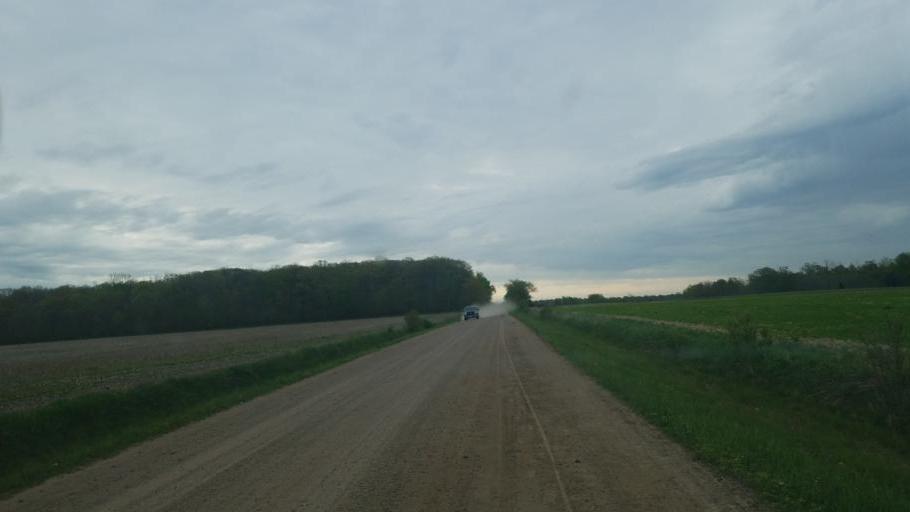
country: US
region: Wisconsin
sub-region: Clark County
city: Loyal
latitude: 44.6255
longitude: -90.4355
